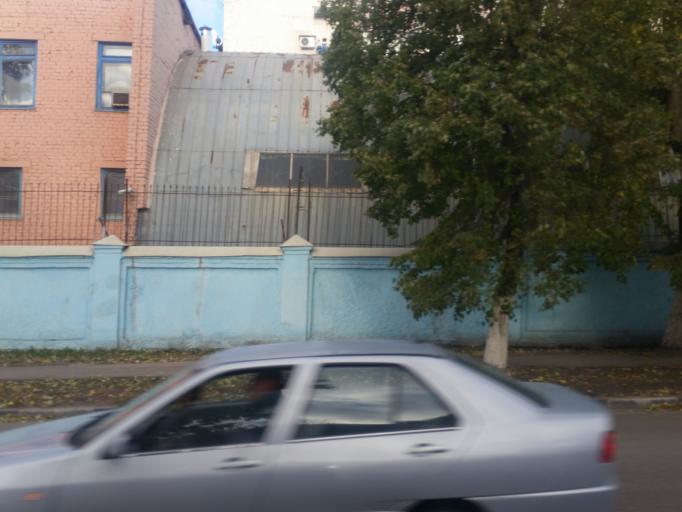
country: RU
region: Ulyanovsk
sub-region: Ulyanovskiy Rayon
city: Ulyanovsk
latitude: 54.3194
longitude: 48.3891
